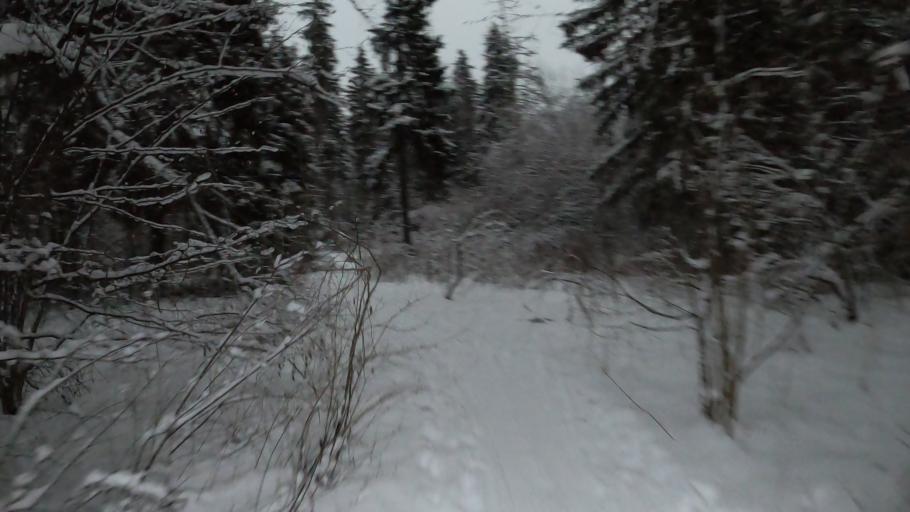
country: RU
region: Moskovskaya
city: Nakhabino
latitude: 55.8931
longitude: 37.2090
